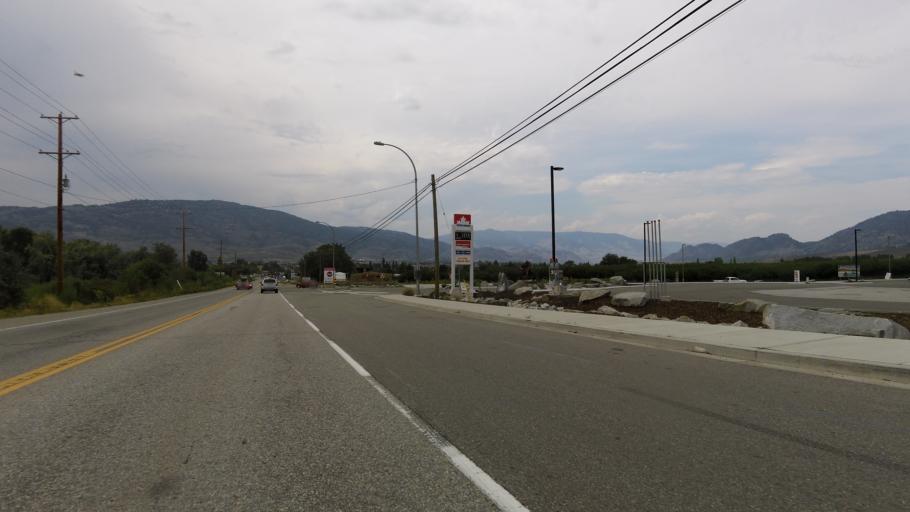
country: CA
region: British Columbia
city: Osoyoos
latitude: 49.0279
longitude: -119.4359
